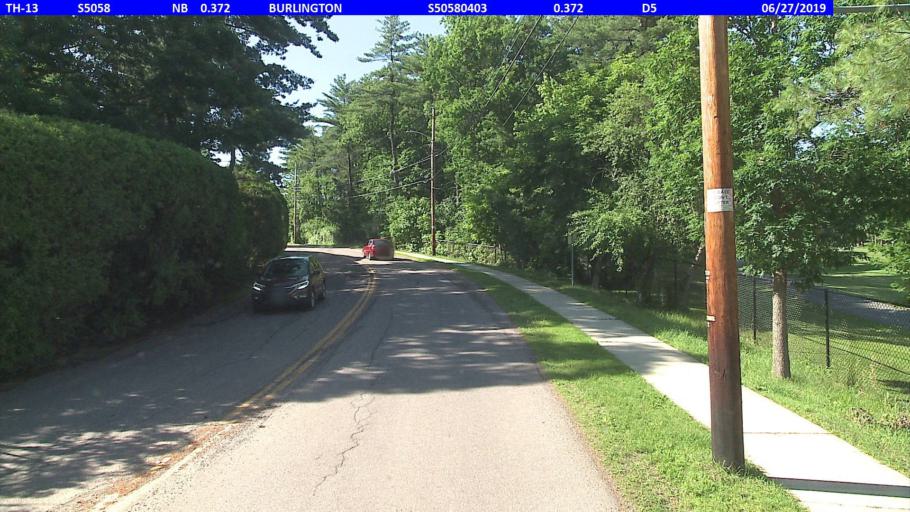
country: US
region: Vermont
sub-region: Chittenden County
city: Burlington
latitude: 44.4628
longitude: -73.2010
